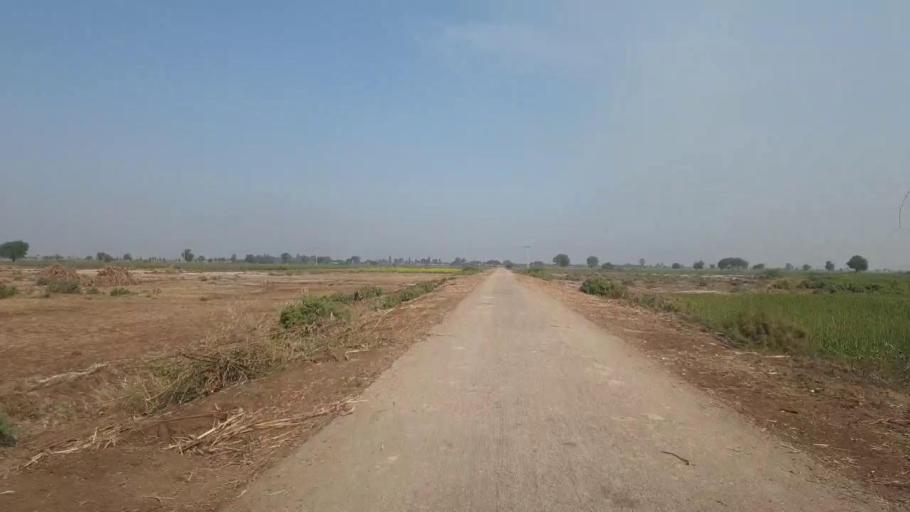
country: PK
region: Sindh
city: Mirwah Gorchani
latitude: 25.3696
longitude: 69.1613
